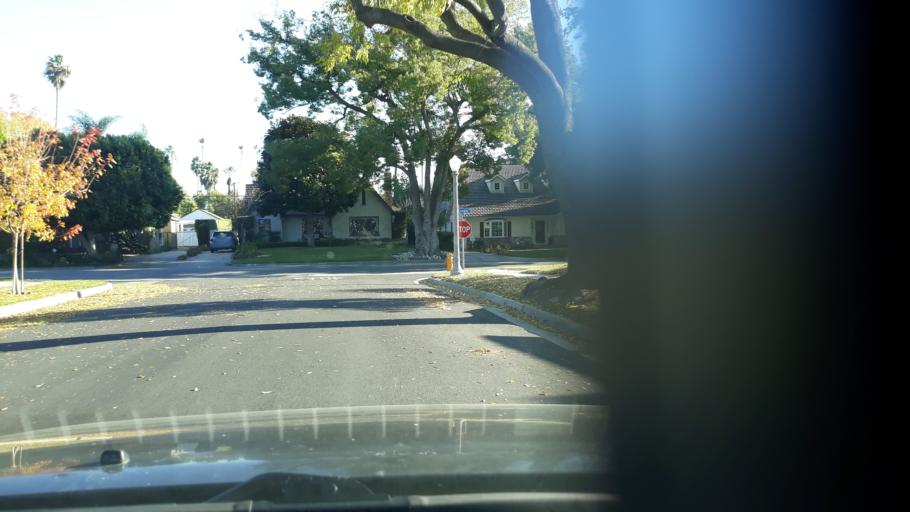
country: US
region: California
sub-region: Los Angeles County
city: San Marino
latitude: 34.1217
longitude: -118.0939
